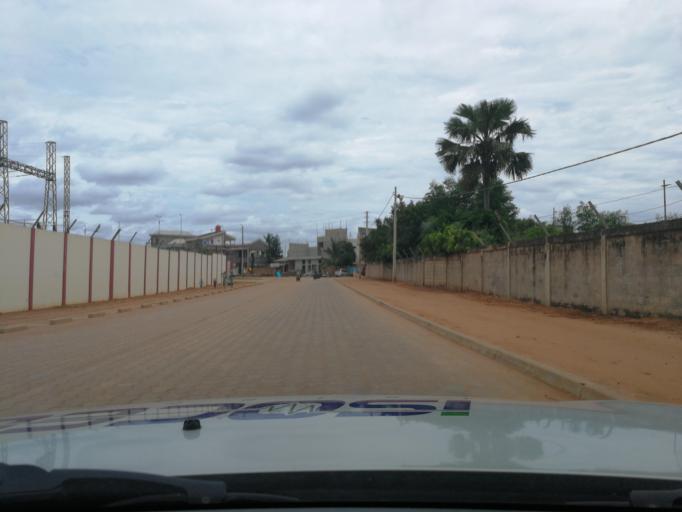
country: BJ
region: Atlantique
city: Abomey-Calavi
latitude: 6.4286
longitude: 2.3061
